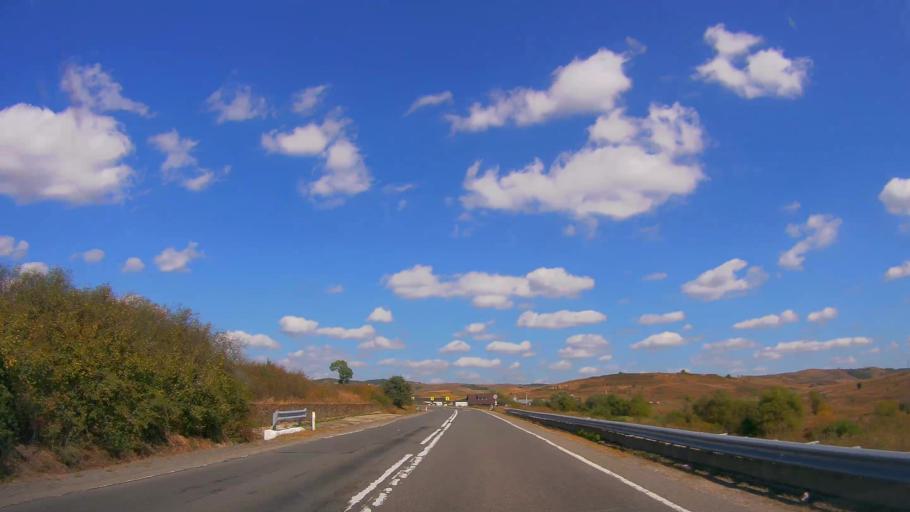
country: RO
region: Cluj
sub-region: Comuna Sanpaul
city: Sanpaul
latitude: 46.9161
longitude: 23.4219
